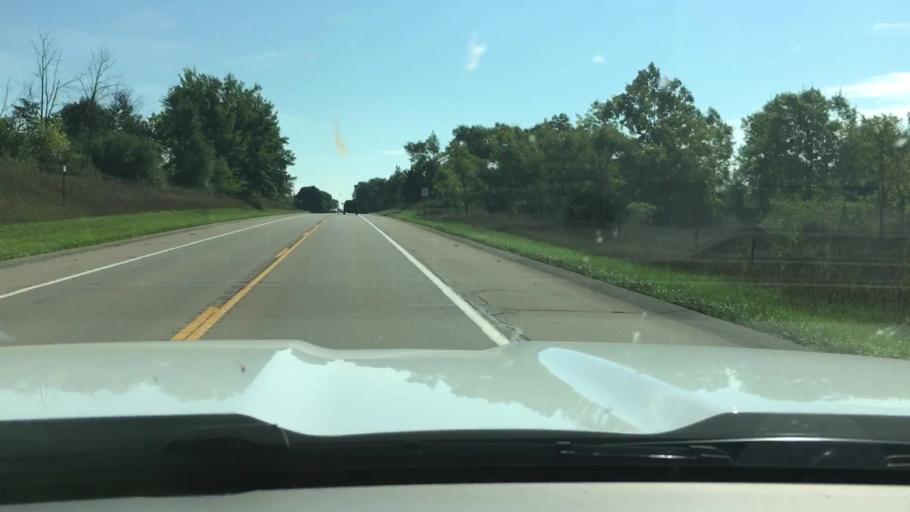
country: US
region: Michigan
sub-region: Gratiot County
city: Alma
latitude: 43.4083
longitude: -84.8296
